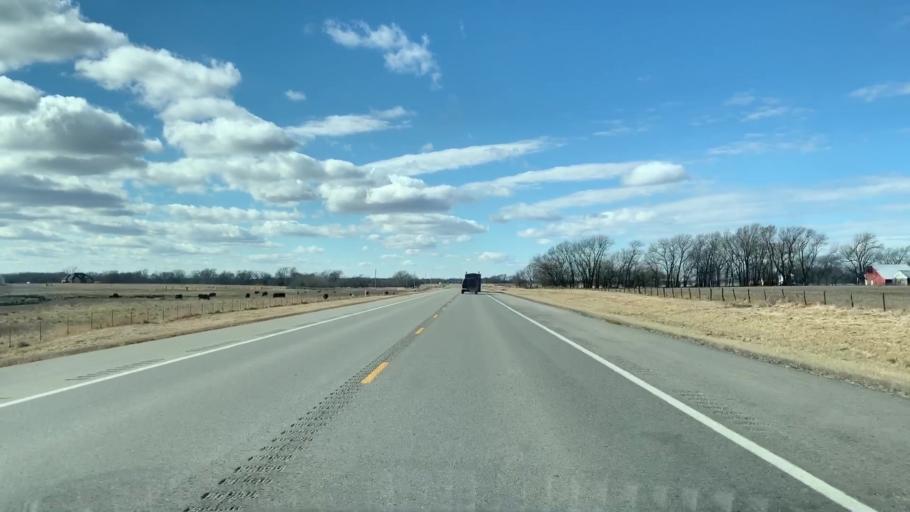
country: US
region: Kansas
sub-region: Crawford County
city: Pittsburg
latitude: 37.3397
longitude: -94.8550
